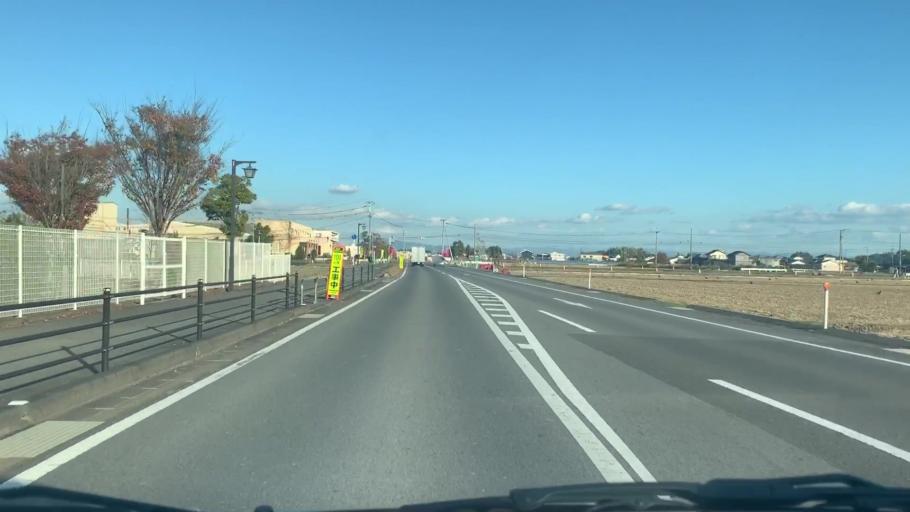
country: JP
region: Saga Prefecture
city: Kanzakimachi-kanzaki
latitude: 33.2677
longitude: 130.3634
